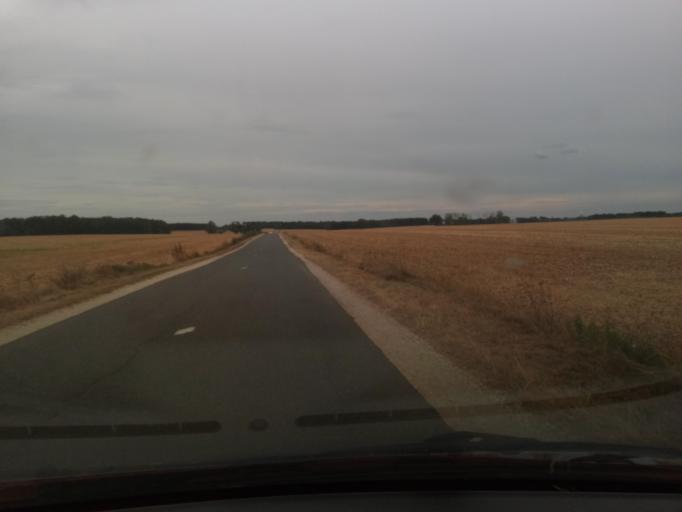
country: FR
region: Poitou-Charentes
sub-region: Departement de la Vienne
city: Saint-Savin
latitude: 46.5705
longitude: 0.7760
